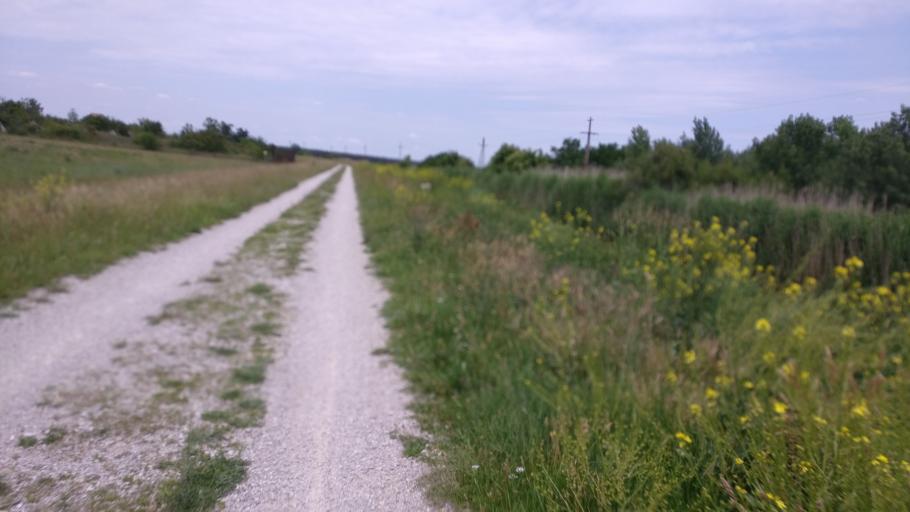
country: AT
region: Lower Austria
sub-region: Politischer Bezirk Wiener Neustadt
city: Lichtenworth
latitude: 47.8502
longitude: 16.2779
